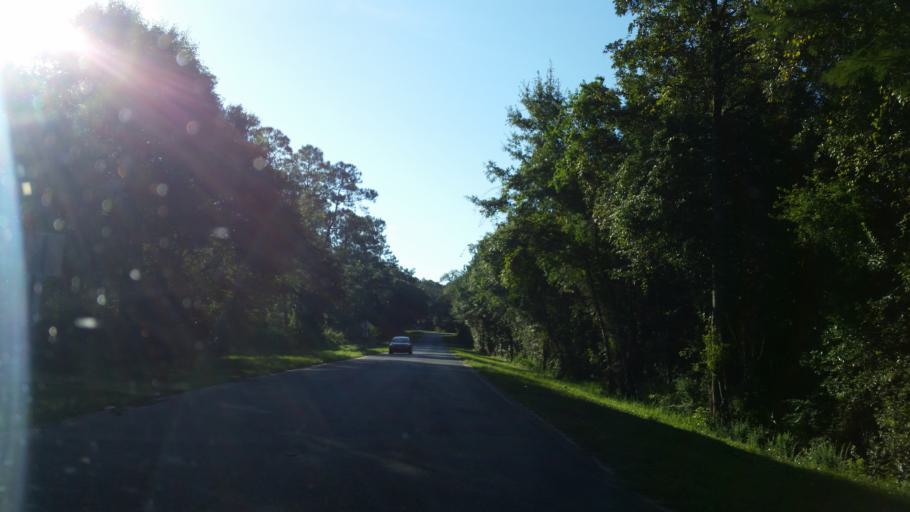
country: US
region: Florida
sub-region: Escambia County
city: Bellview
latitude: 30.4850
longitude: -87.3330
